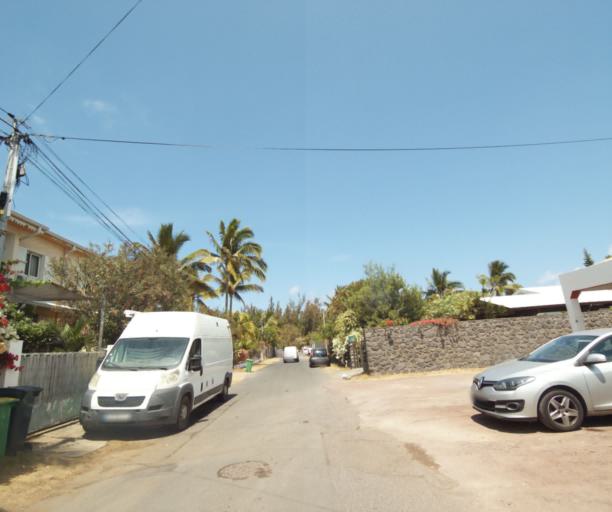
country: RE
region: Reunion
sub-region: Reunion
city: Trois-Bassins
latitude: -21.0878
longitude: 55.2327
